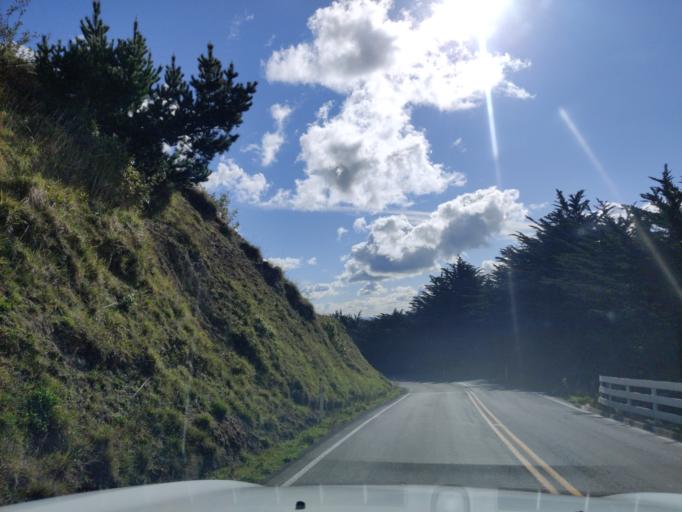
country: NZ
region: Manawatu-Wanganui
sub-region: Palmerston North City
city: Palmerston North
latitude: -40.2871
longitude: 175.7927
